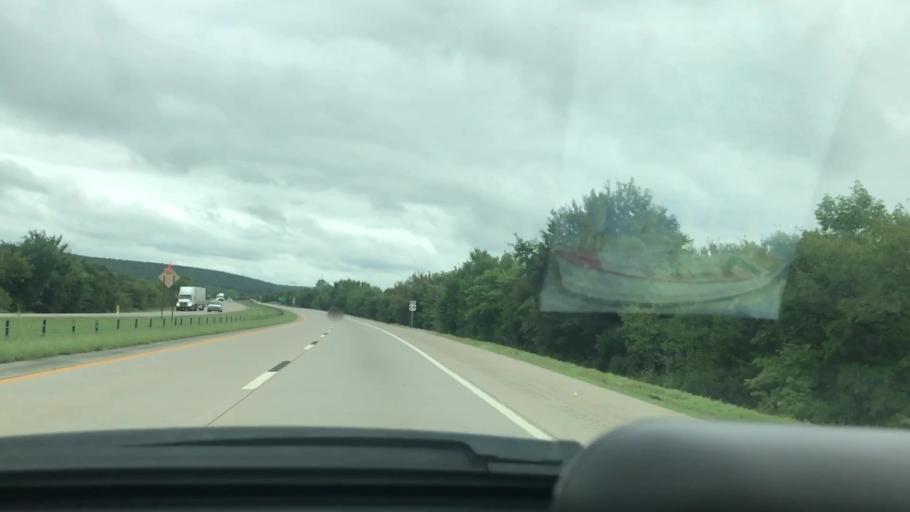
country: US
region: Oklahoma
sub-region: Pittsburg County
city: Krebs
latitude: 35.0057
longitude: -95.7190
